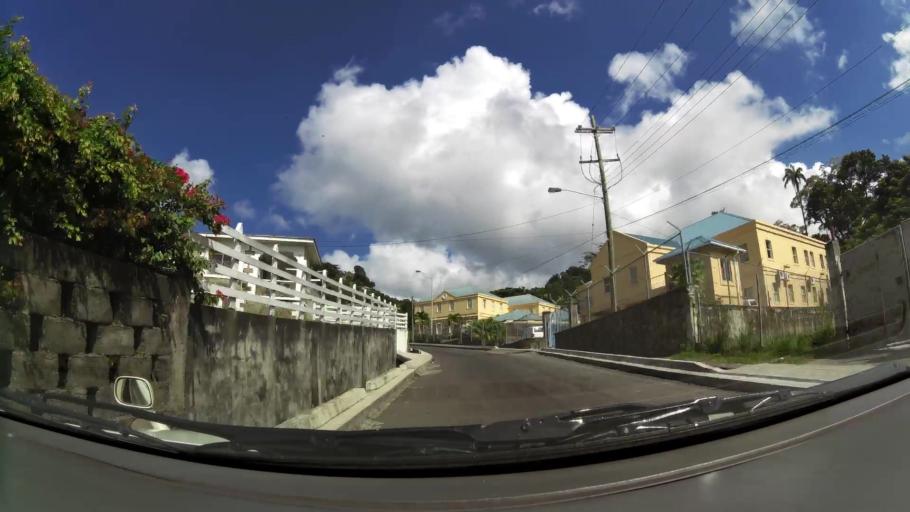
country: VC
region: Saint George
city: Kingstown
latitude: 13.1641
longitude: -61.2285
